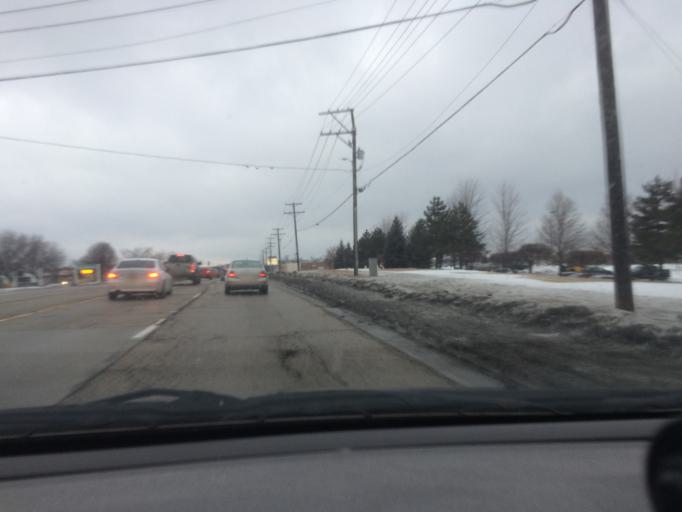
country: US
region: Illinois
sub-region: DuPage County
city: Hanover Park
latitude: 41.9756
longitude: -88.1269
